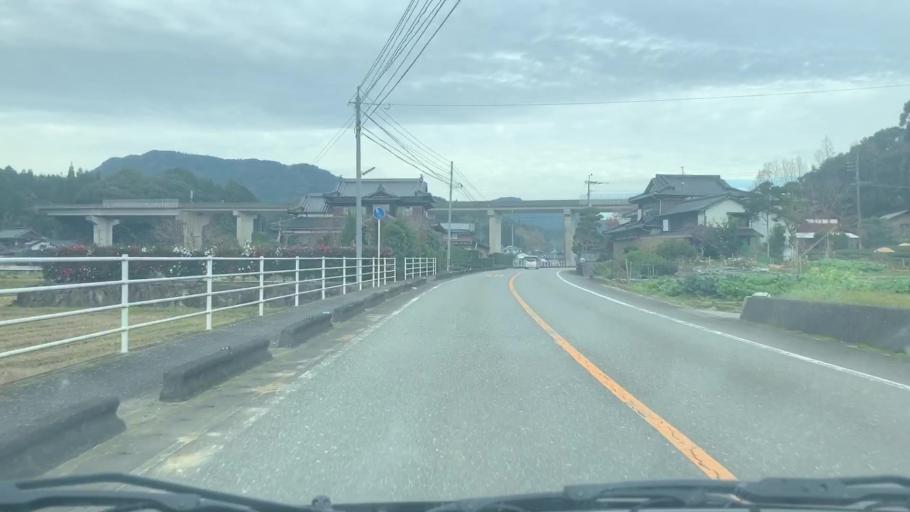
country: JP
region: Saga Prefecture
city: Ureshinomachi-shimojuku
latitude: 33.1417
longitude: 129.9772
